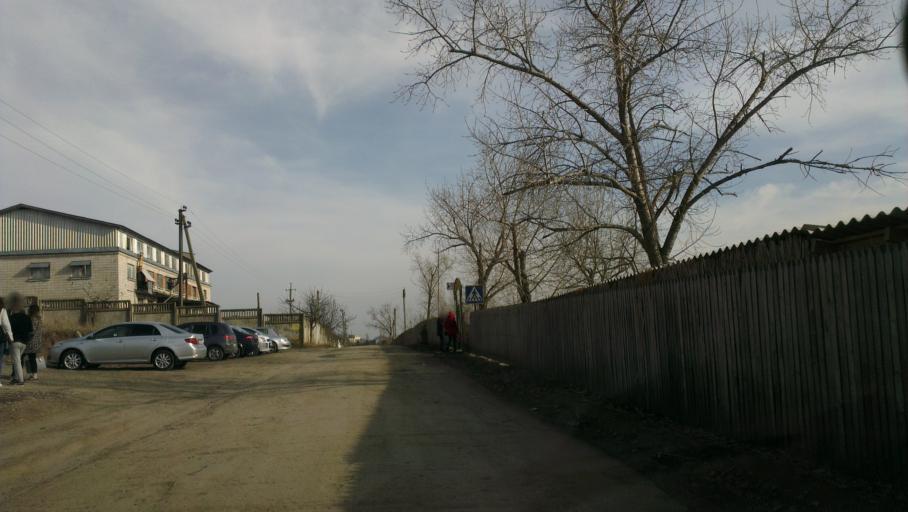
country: MD
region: Laloveni
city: Ialoveni
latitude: 46.9132
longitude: 28.7017
